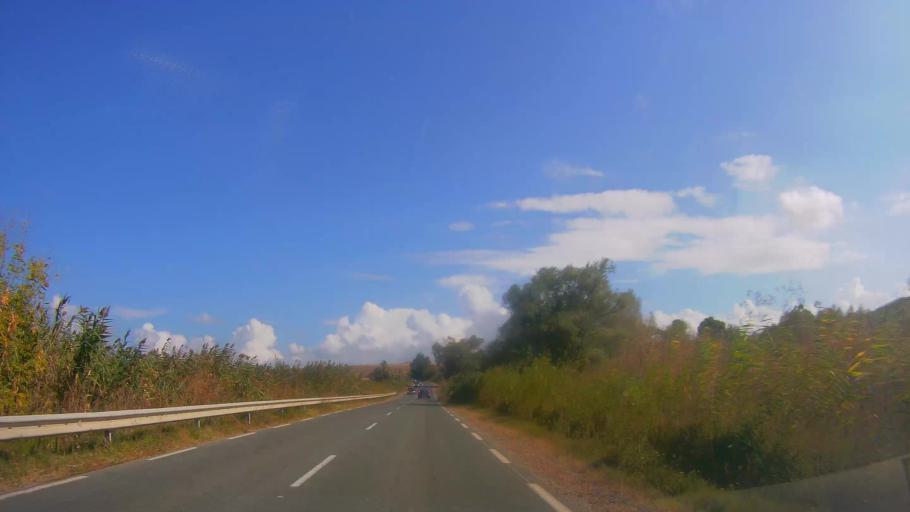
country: BG
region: Burgas
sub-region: Obshtina Burgas
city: Burgas
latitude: 42.4747
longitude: 27.3600
